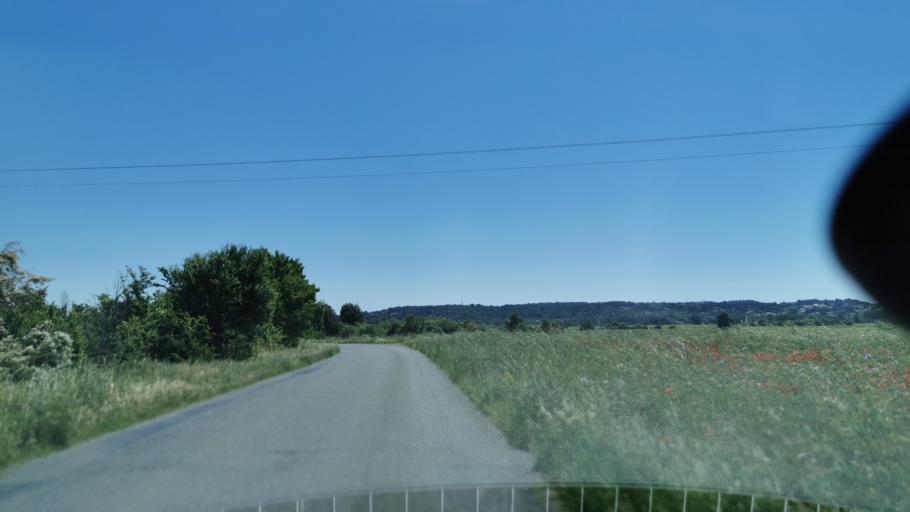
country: FR
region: Languedoc-Roussillon
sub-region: Departement de l'Aude
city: Marcorignan
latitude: 43.2437
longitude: 2.9119
